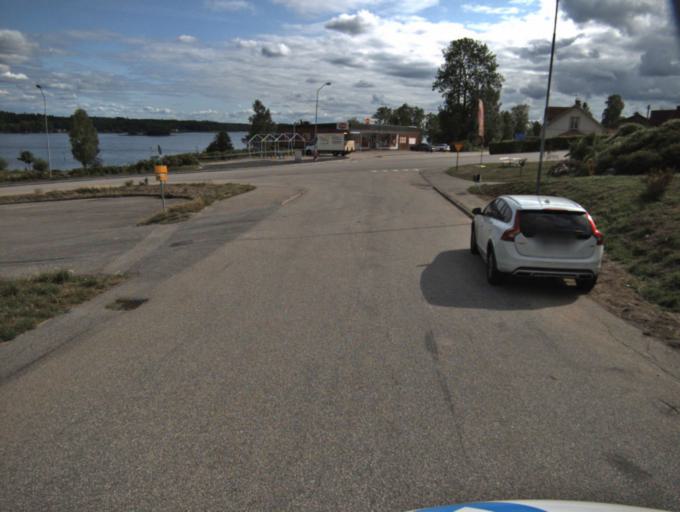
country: SE
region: Vaestra Goetaland
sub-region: Ulricehamns Kommun
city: Ulricehamn
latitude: 57.6795
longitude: 13.3750
